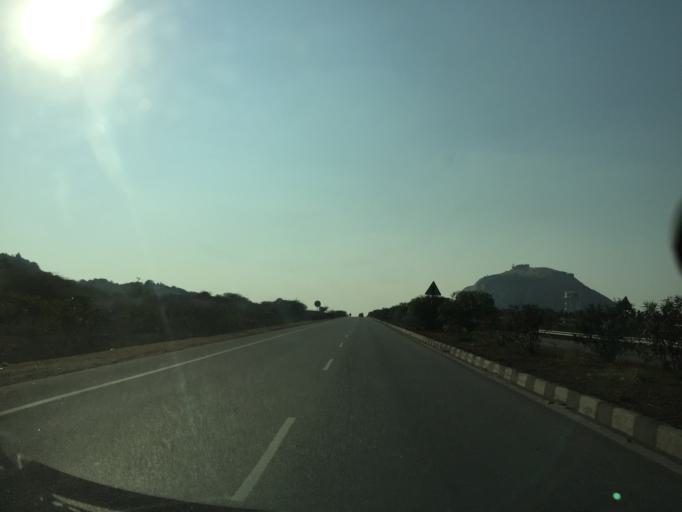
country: IN
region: Telangana
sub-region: Nalgonda
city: Bhongir
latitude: 17.5136
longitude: 78.9082
